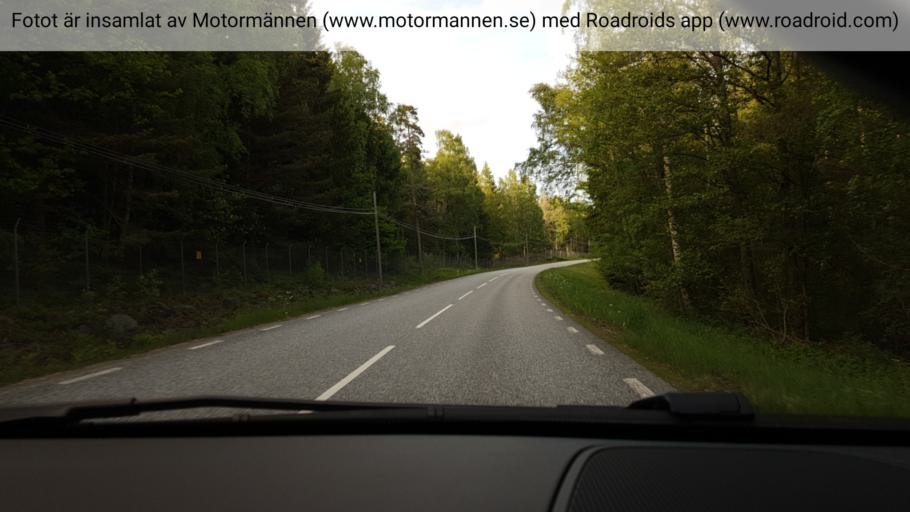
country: SE
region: Stockholm
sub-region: Nynashamns Kommun
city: Nynashamn
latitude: 58.9785
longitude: 18.0821
